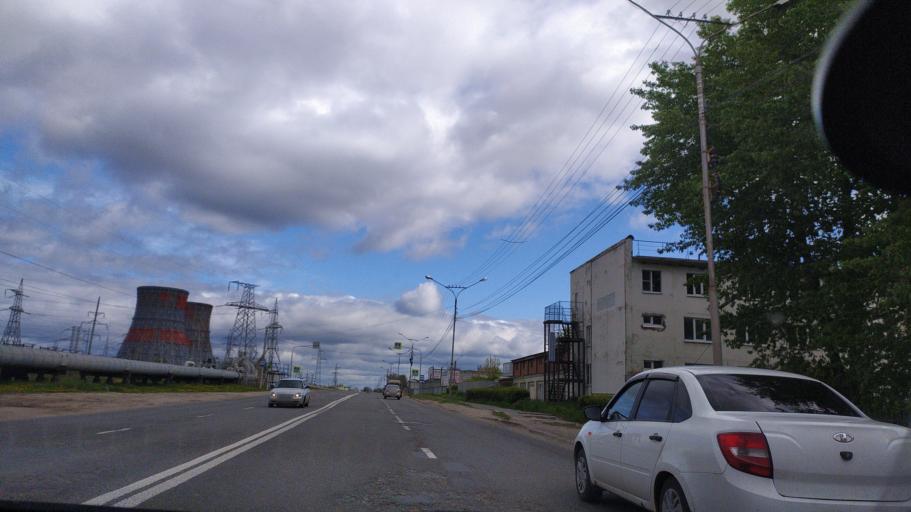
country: RU
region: Chuvashia
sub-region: Cheboksarskiy Rayon
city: Cheboksary
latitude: 56.1201
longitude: 47.3023
